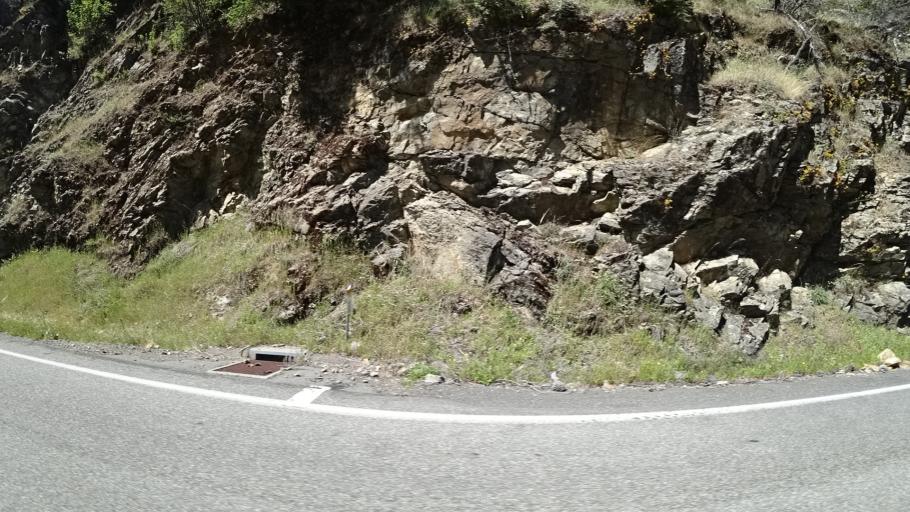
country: US
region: California
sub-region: Trinity County
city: Hayfork
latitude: 40.7476
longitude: -123.1711
